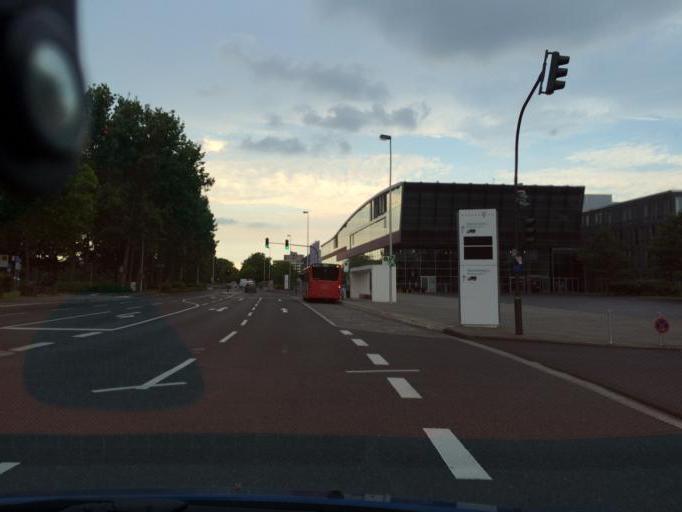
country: DE
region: North Rhine-Westphalia
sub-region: Regierungsbezirk Koln
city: Bonn
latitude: 50.7223
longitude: 7.1440
